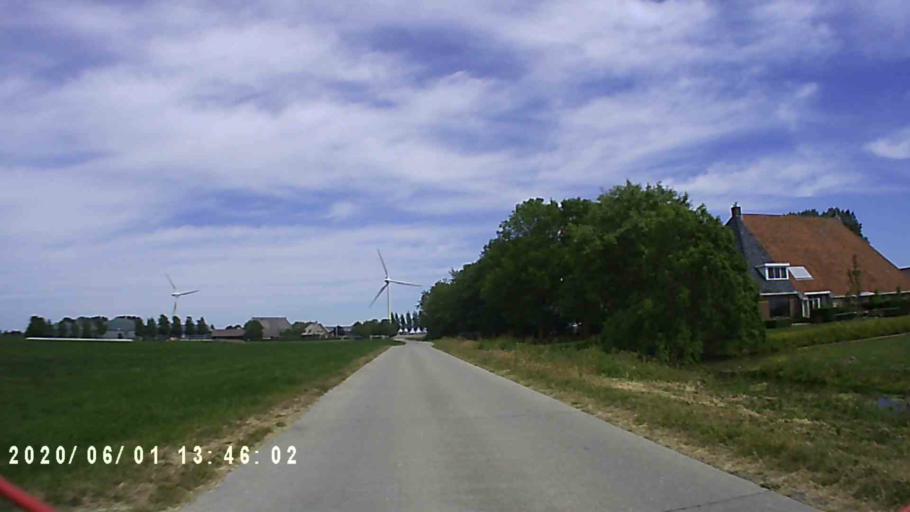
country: NL
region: Friesland
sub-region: Gemeente Littenseradiel
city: Wommels
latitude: 53.0910
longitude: 5.6229
